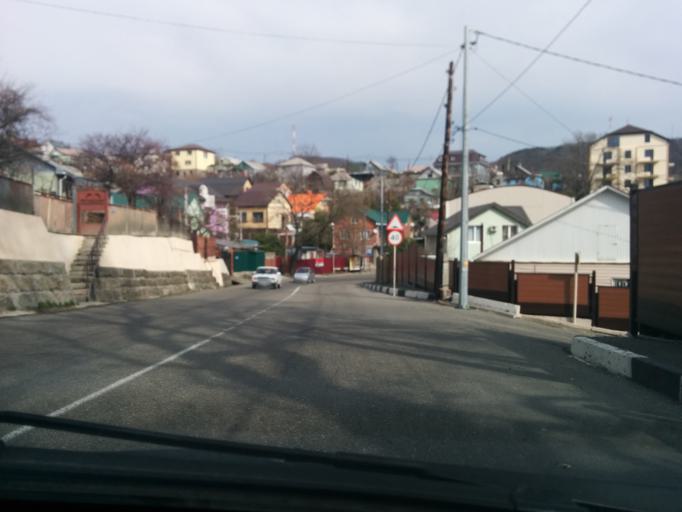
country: RU
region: Krasnodarskiy
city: Tuapse
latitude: 44.1039
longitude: 39.0666
